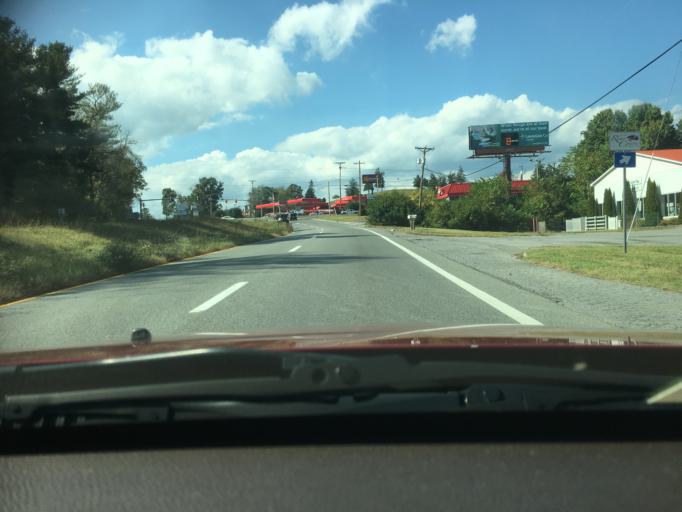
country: US
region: Virginia
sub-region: Pulaski County
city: Fairlawn
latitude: 37.1459
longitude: -80.5847
